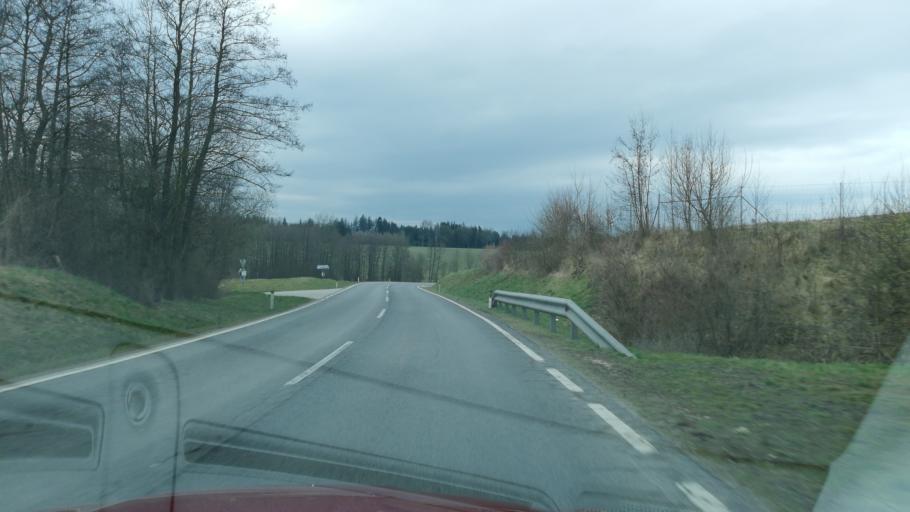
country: AT
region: Upper Austria
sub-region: Wels-Land
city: Offenhausen
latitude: 48.1789
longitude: 13.7772
